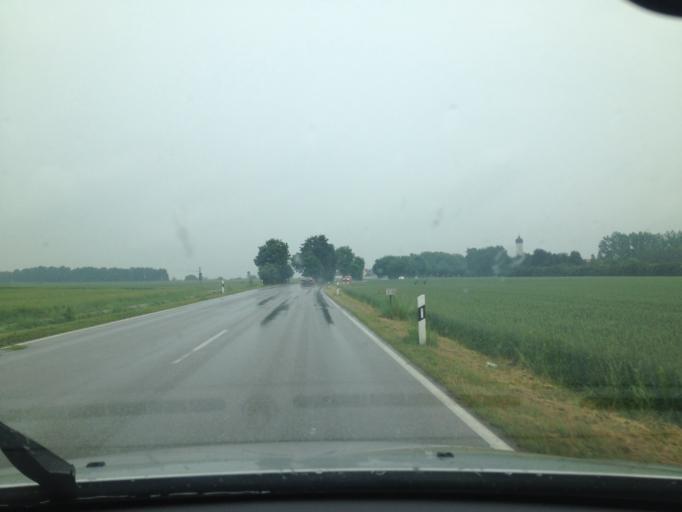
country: DE
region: Bavaria
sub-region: Swabia
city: Untermeitingen
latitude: 48.1643
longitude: 10.7978
